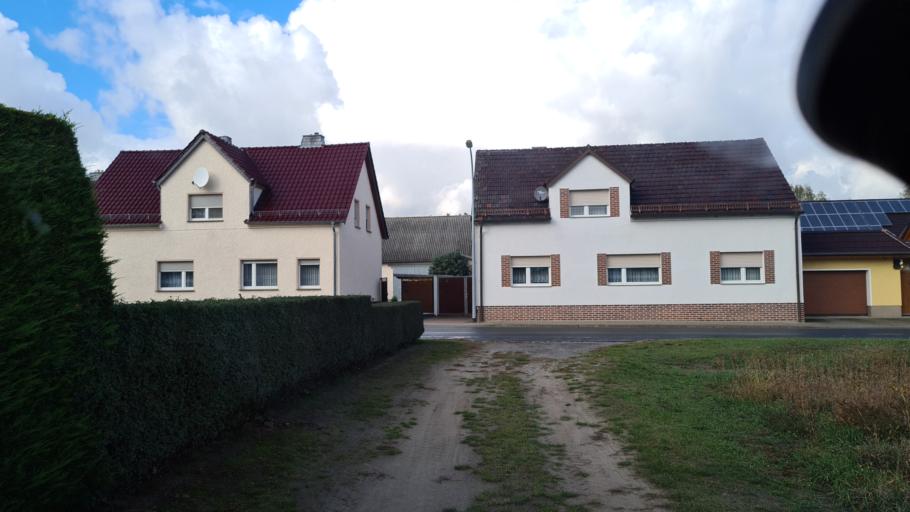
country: DE
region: Brandenburg
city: Schonewalde
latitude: 51.6994
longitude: 13.5769
